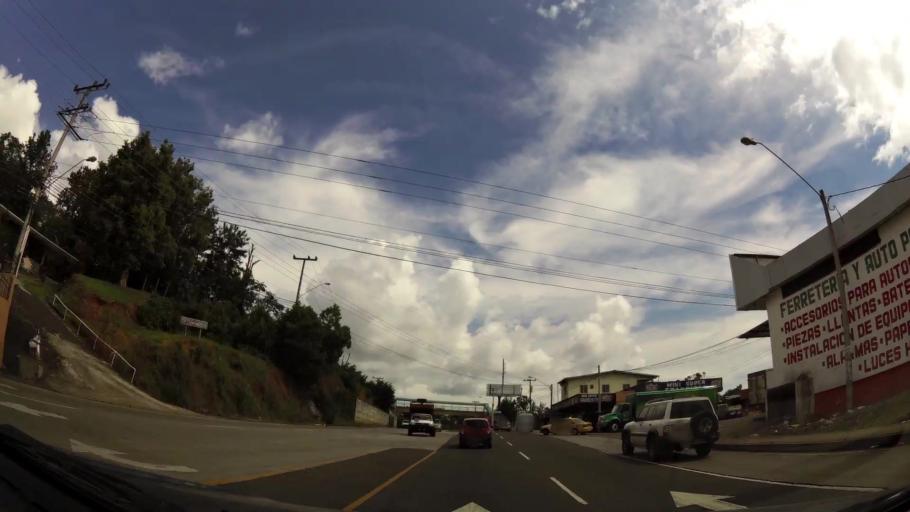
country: PA
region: Panama
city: Vista Alegre
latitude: 8.9353
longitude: -79.6869
